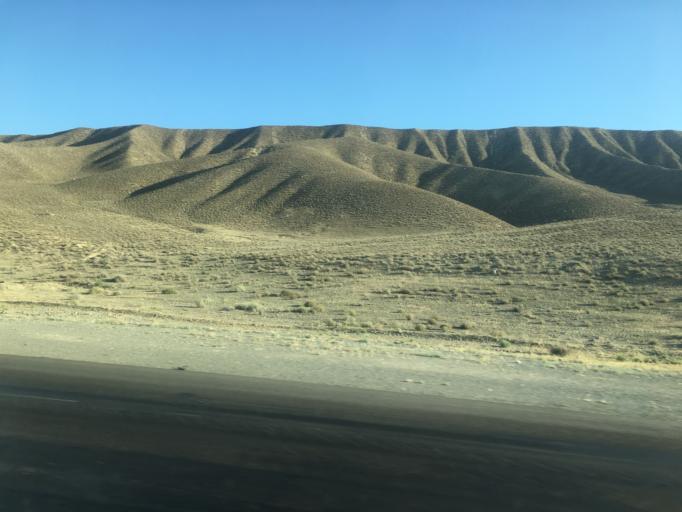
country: TM
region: Ahal
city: Baharly
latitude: 38.6026
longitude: 57.0710
